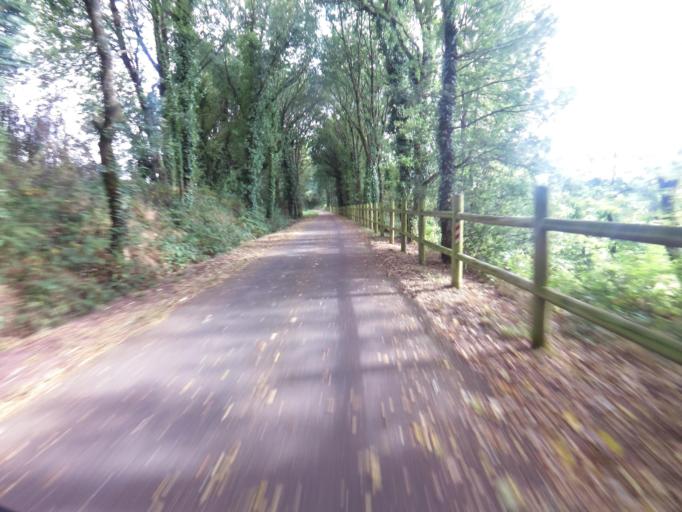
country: FR
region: Brittany
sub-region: Departement du Morbihan
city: Guillac
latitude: 47.8971
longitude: -2.4364
